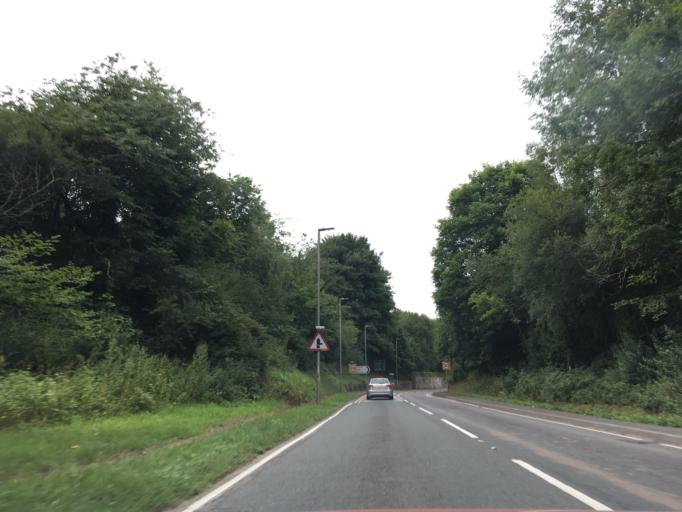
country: GB
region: Wales
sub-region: Sir Powys
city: Cray
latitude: 51.9499
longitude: -3.5631
